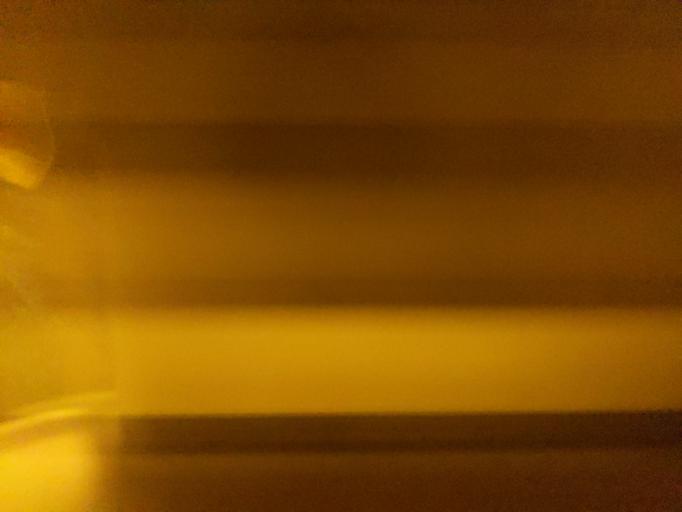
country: JP
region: Fukushima
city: Sukagawa
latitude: 37.2293
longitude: 140.2862
